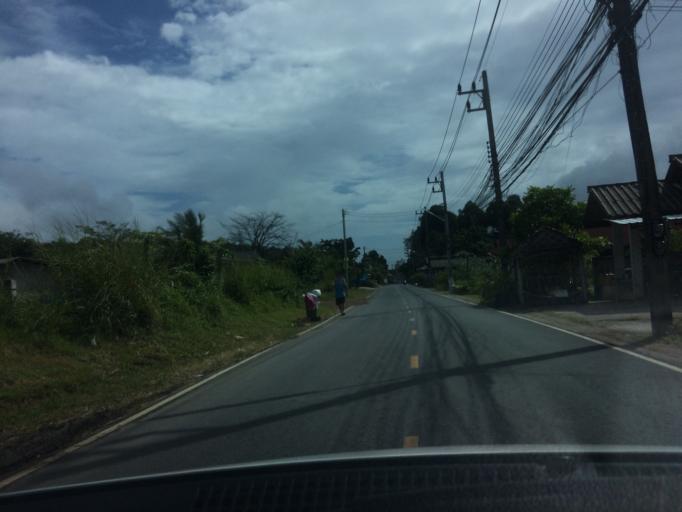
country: TH
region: Phuket
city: Thalang
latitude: 8.0289
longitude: 98.3381
